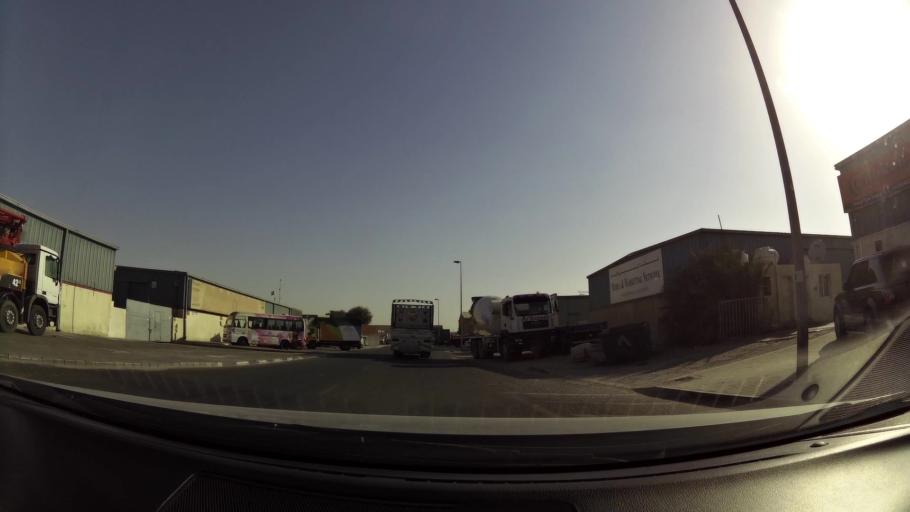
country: AE
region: Dubai
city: Dubai
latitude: 25.1229
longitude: 55.2383
